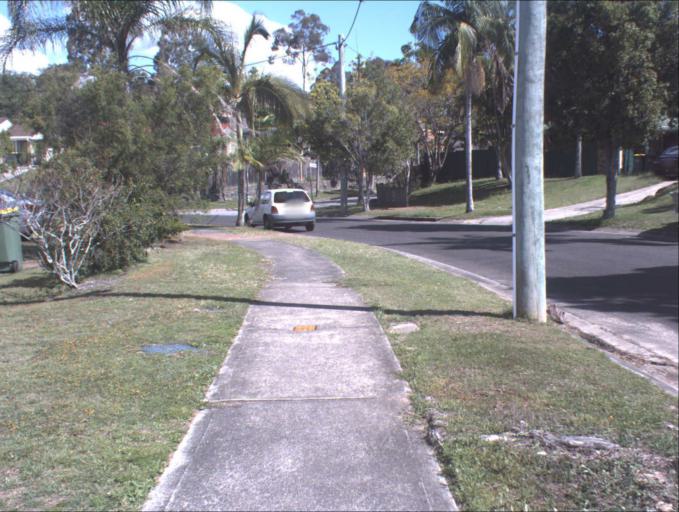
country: AU
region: Queensland
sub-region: Logan
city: Waterford West
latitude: -27.7036
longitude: 153.1665
